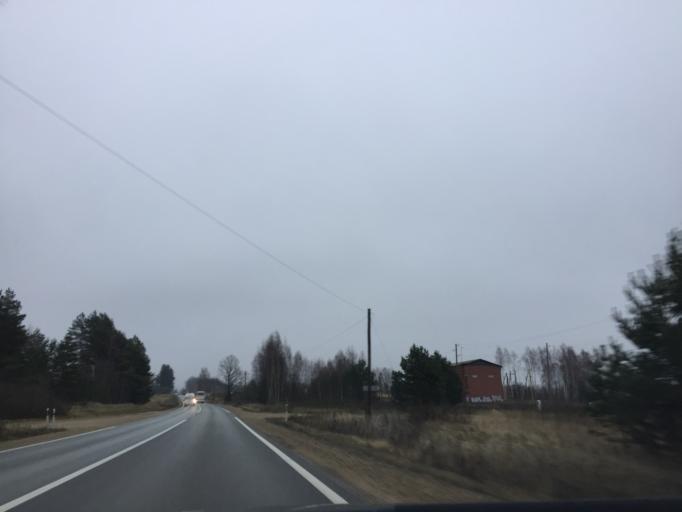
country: LV
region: Pargaujas
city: Stalbe
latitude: 57.3697
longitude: 25.0060
